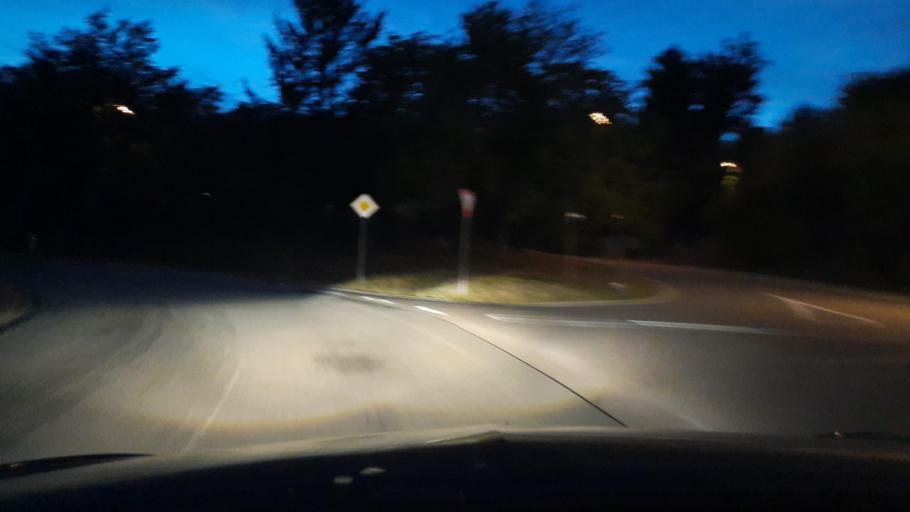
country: DE
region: Rheinland-Pfalz
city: Korlingen
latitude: 49.7270
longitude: 6.7243
